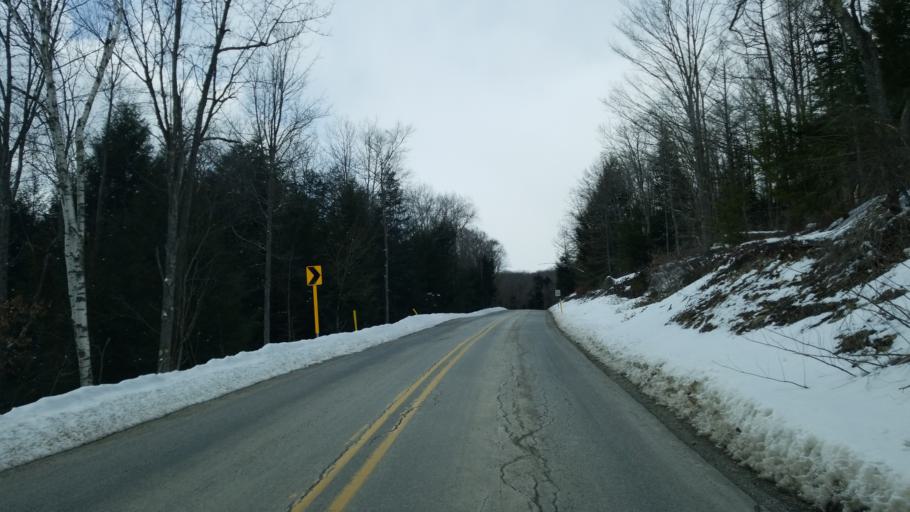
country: US
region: Pennsylvania
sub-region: Clearfield County
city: Shiloh
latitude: 41.2394
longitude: -78.1777
